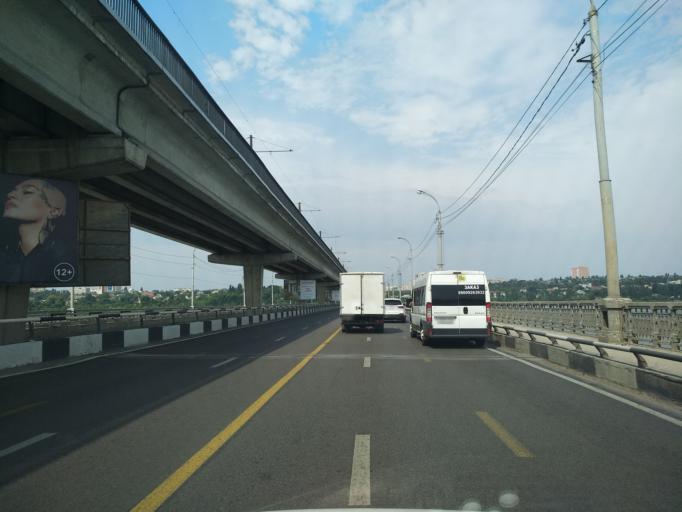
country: RU
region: Voronezj
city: Voronezh
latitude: 51.6904
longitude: 39.2458
